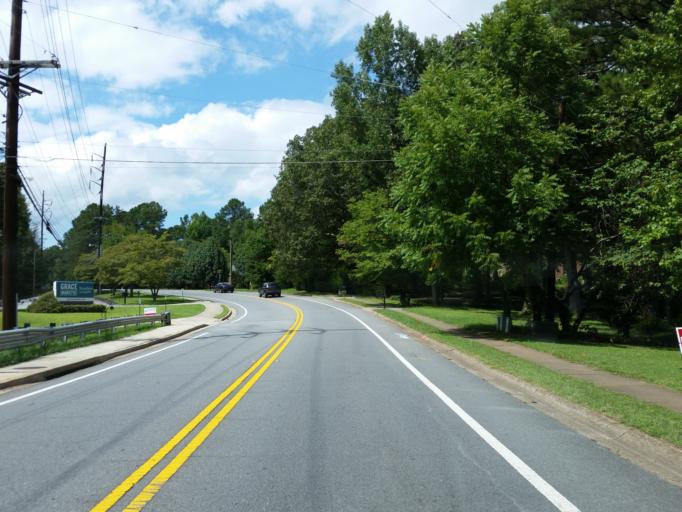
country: US
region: Georgia
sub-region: Cobb County
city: Marietta
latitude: 33.9662
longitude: -84.4793
